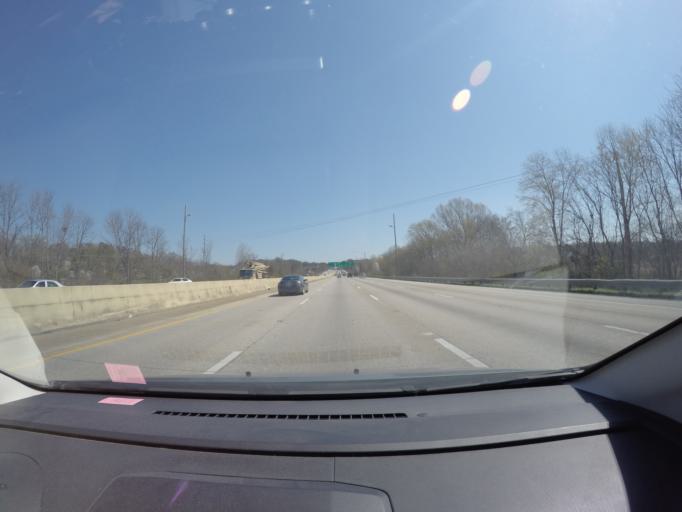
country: US
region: Tennessee
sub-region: Hamilton County
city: East Brainerd
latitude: 35.0090
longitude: -85.1970
